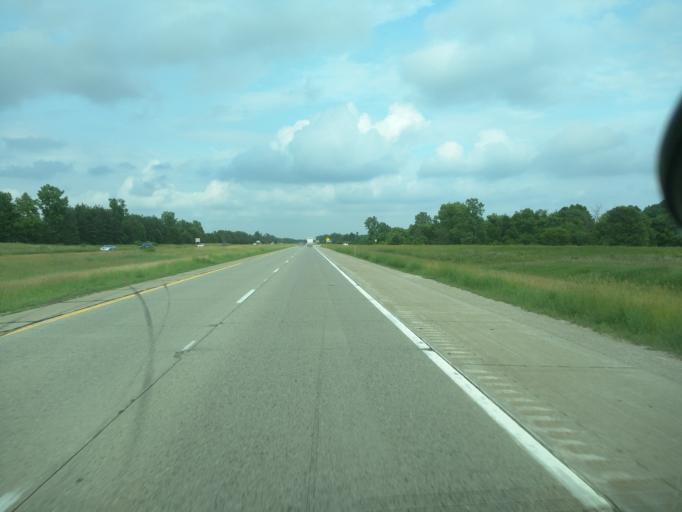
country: US
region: Michigan
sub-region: Clinton County
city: DeWitt
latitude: 42.8164
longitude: -84.5699
